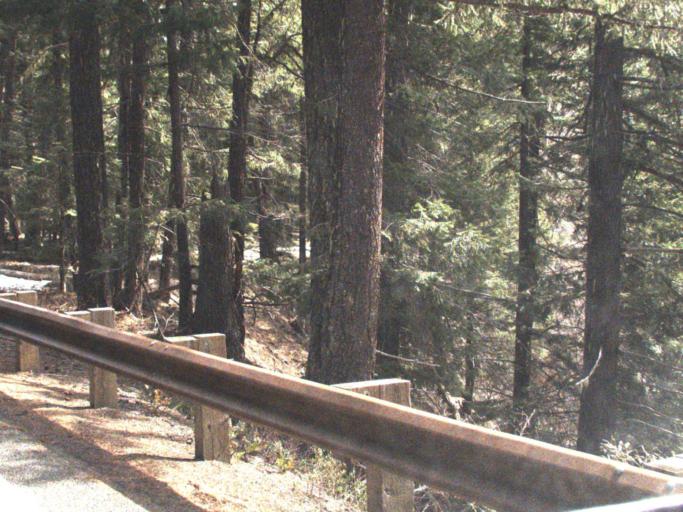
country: US
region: Washington
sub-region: Kittitas County
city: Cle Elum
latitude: 46.9775
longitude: -121.1786
